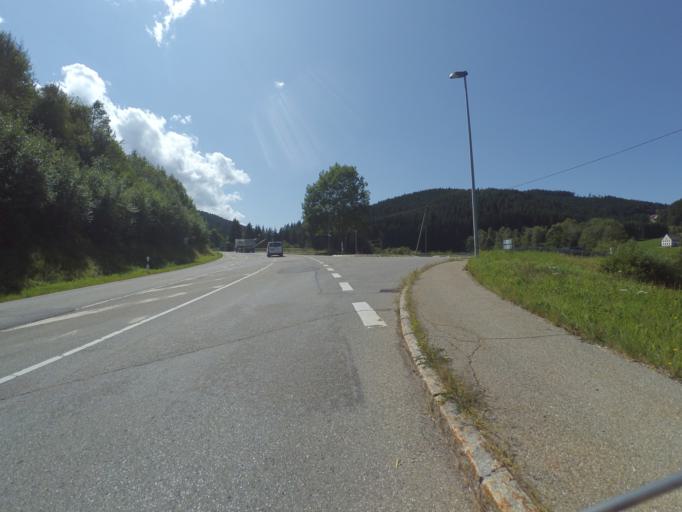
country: DE
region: Baden-Wuerttemberg
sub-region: Freiburg Region
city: Eisenbach
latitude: 47.9934
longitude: 8.3135
